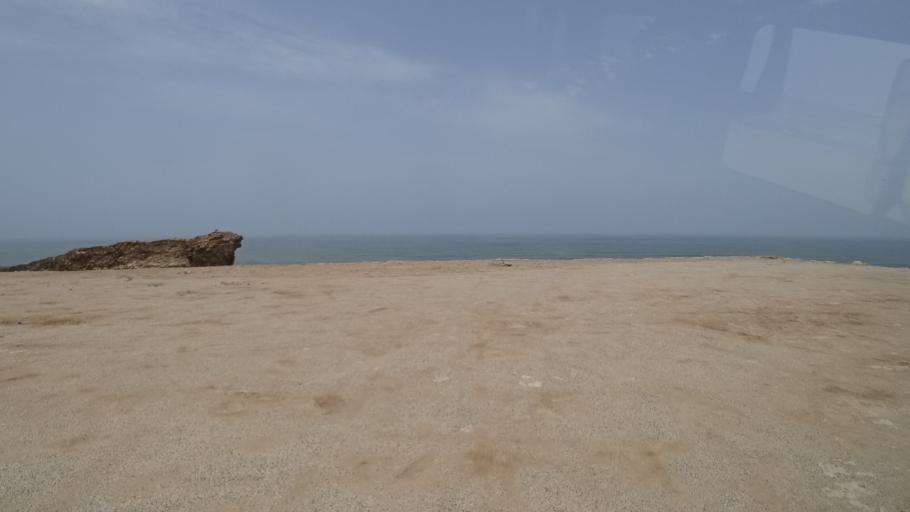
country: OM
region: Zufar
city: Salalah
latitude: 17.0322
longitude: 54.4103
